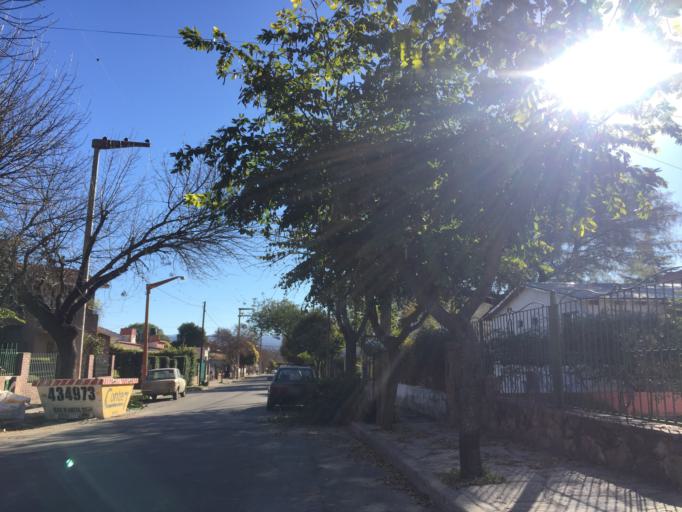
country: AR
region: Cordoba
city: Villa Carlos Paz
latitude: -31.4287
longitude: -64.4928
